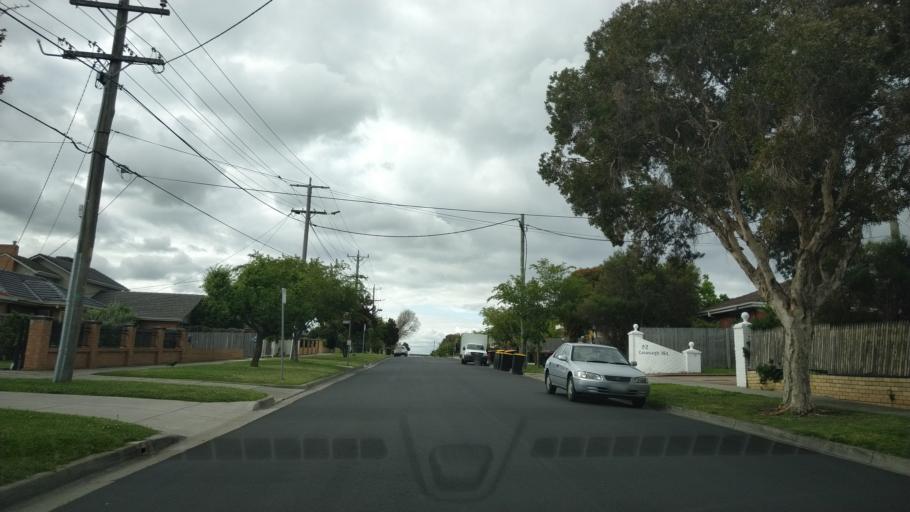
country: AU
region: Victoria
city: Highett
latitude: -37.9572
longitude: 145.0666
